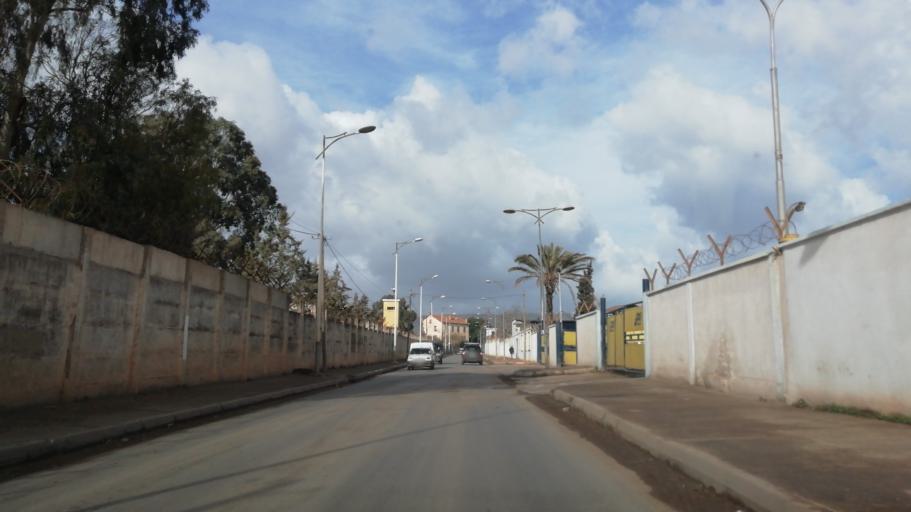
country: DZ
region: Oran
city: Oran
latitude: 35.6784
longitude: -0.6223
